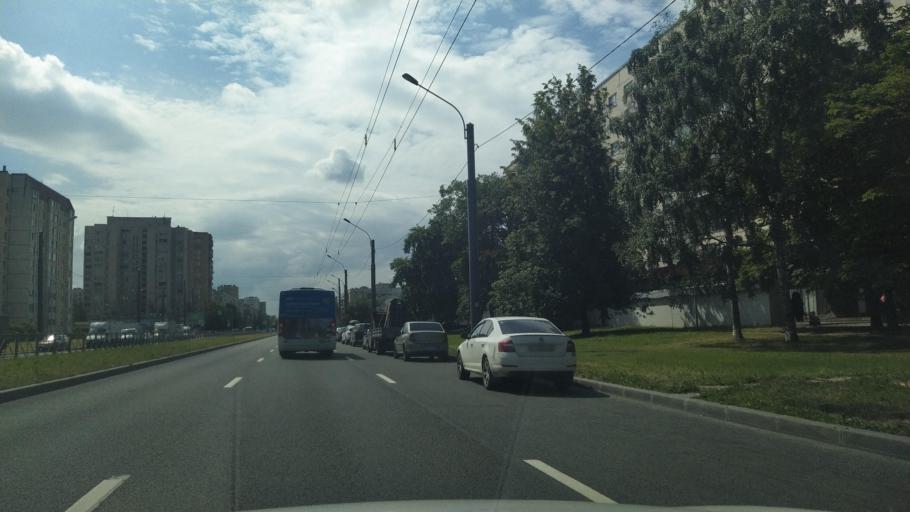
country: RU
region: Leningrad
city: Parnas
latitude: 60.0510
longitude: 30.3557
